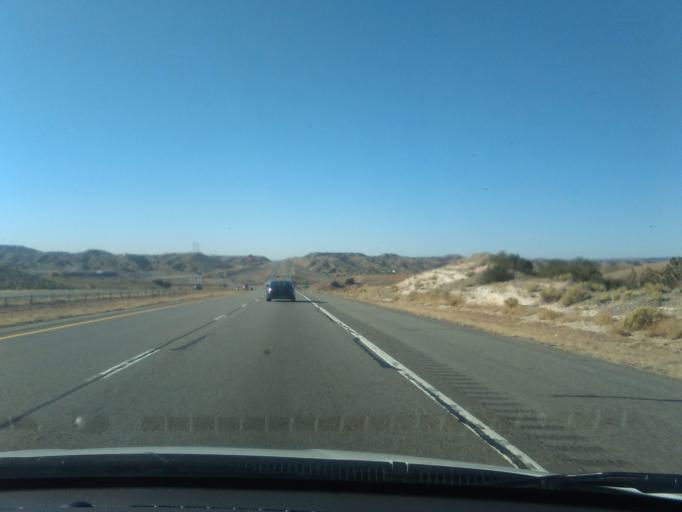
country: US
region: New Mexico
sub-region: Sandoval County
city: San Felipe Pueblo
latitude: 35.4238
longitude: -106.3944
